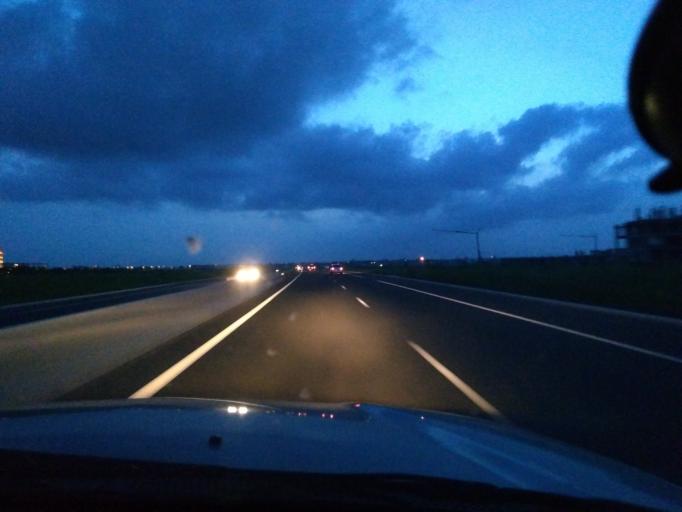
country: SN
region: Thies
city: Thies
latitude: 14.7354
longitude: -17.1993
